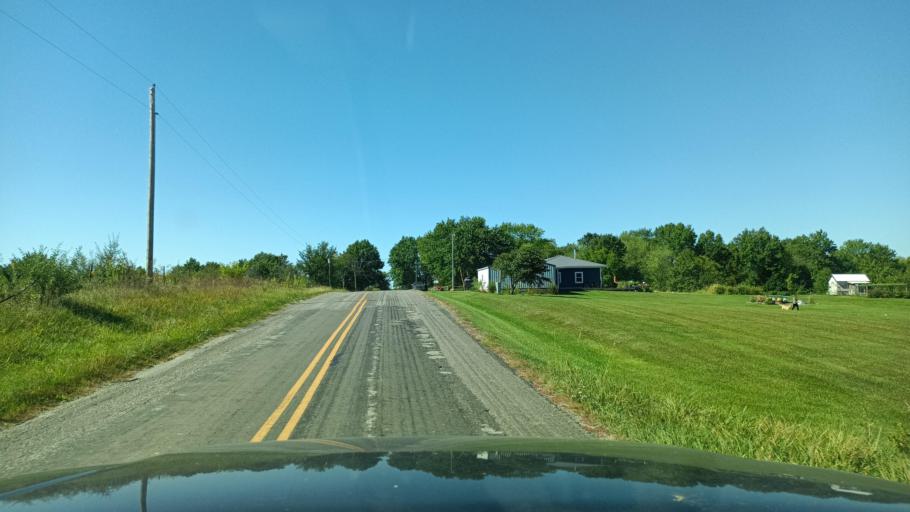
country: US
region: Missouri
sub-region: Scotland County
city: Memphis
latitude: 40.3553
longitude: -92.2623
